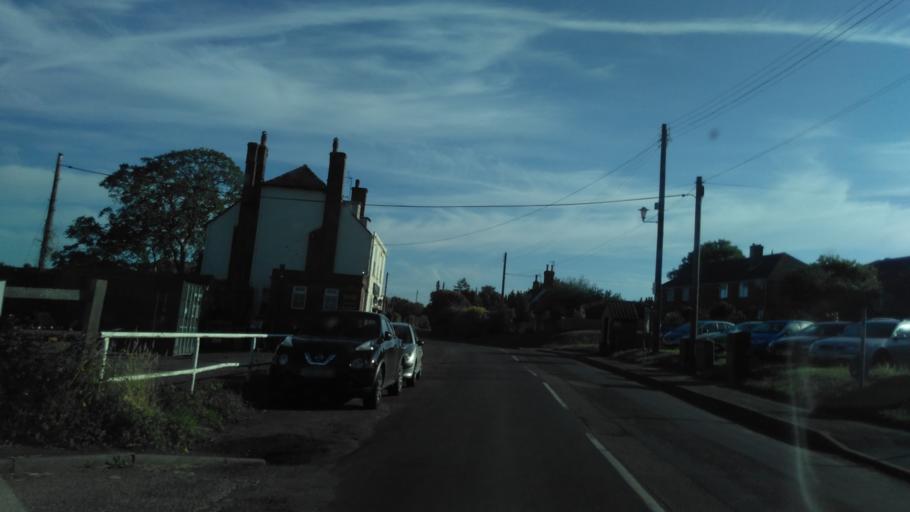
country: GB
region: England
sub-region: Kent
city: Dunkirk
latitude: 51.3199
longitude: 0.9408
